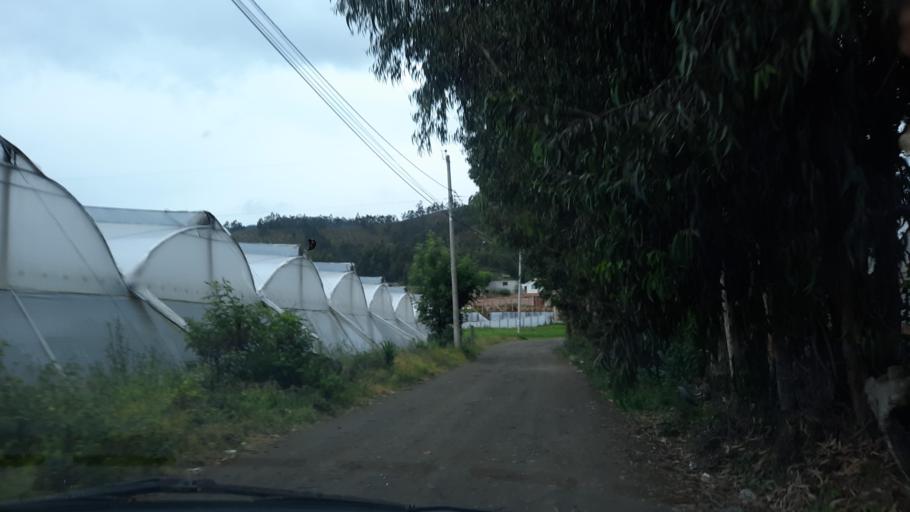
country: EC
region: Chimborazo
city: Riobamba
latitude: -1.6866
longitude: -78.6581
